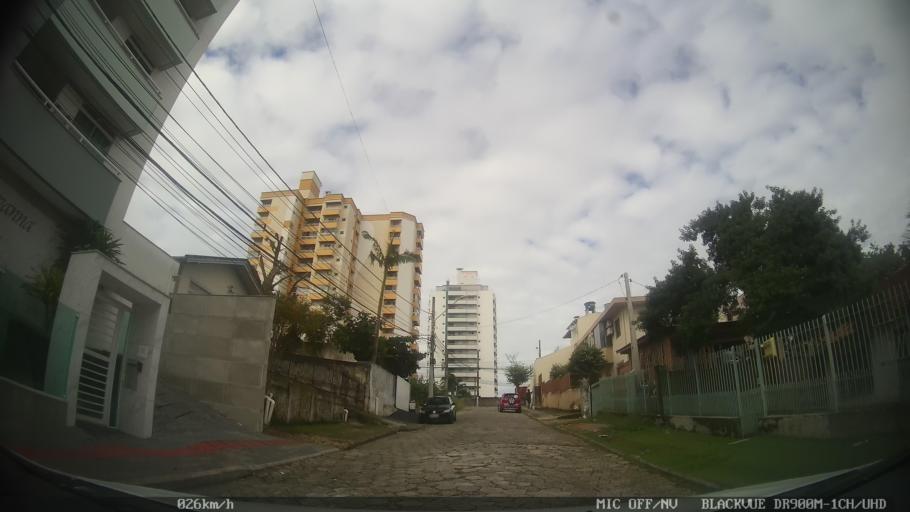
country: BR
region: Santa Catarina
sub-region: Sao Jose
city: Campinas
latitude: -27.5771
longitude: -48.6083
